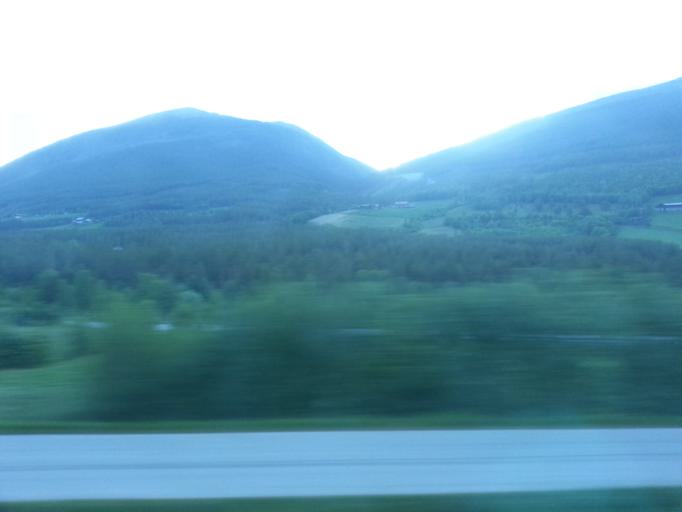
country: NO
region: Oppland
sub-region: Dovre
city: Dovre
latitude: 61.9190
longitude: 9.3429
